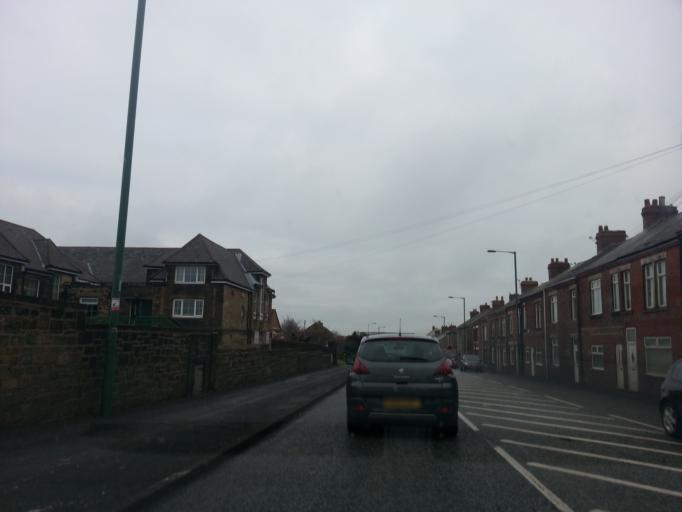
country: GB
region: England
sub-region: County Durham
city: Stanley
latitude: 54.8657
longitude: -1.7110
